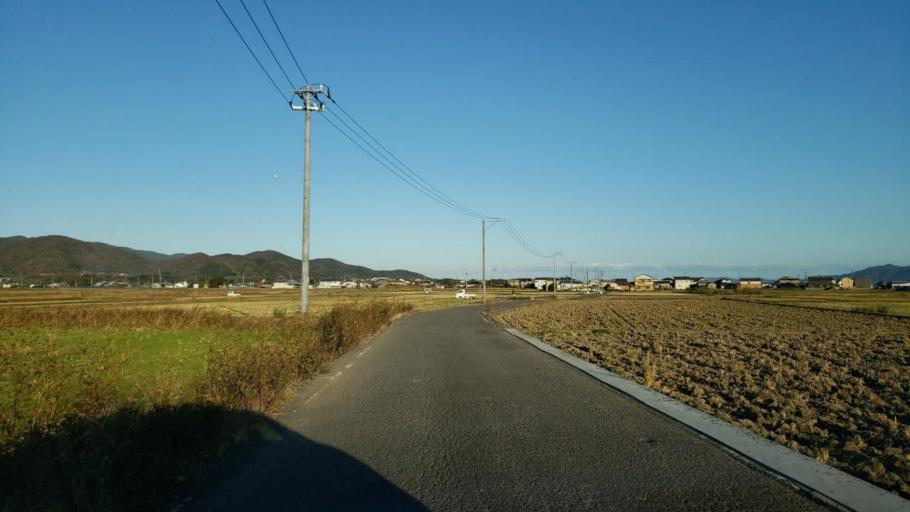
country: JP
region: Tokushima
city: Kamojimacho-jogejima
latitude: 34.0909
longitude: 134.2592
